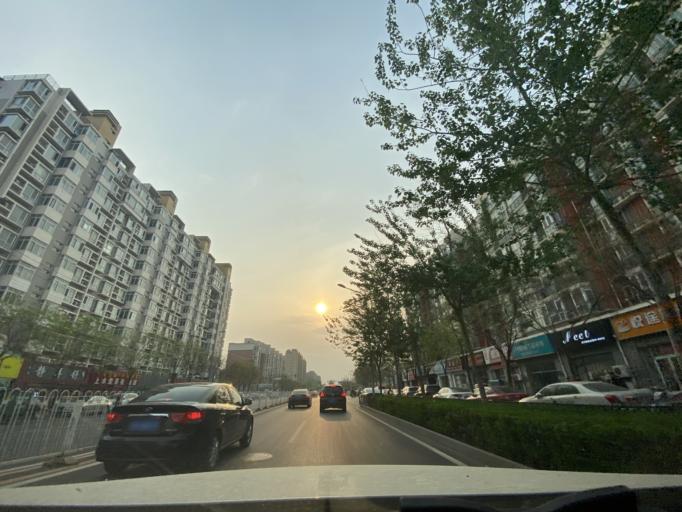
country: CN
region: Beijing
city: Babaoshan
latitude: 39.9283
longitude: 116.2438
